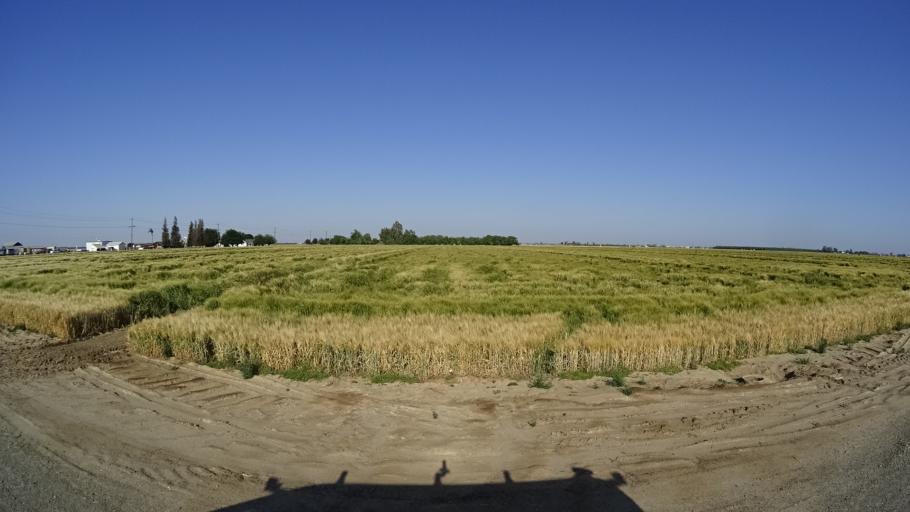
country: US
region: California
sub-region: Kings County
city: Home Garden
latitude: 36.2997
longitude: -119.5652
